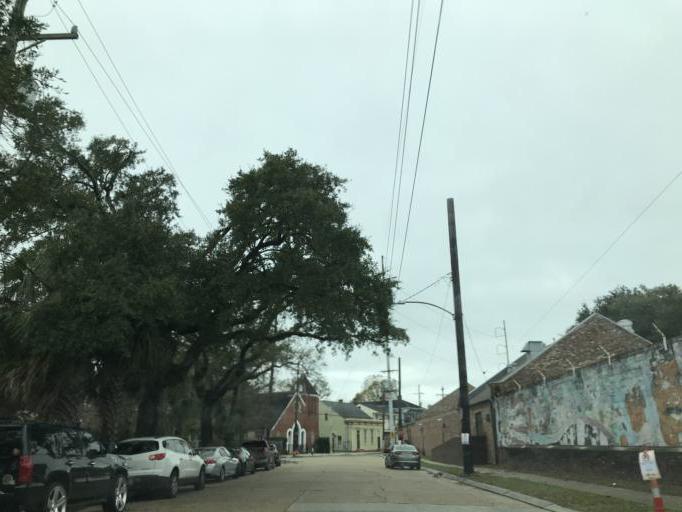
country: US
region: Louisiana
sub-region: Jefferson Parish
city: Gretna
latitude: 29.9309
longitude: -90.0710
